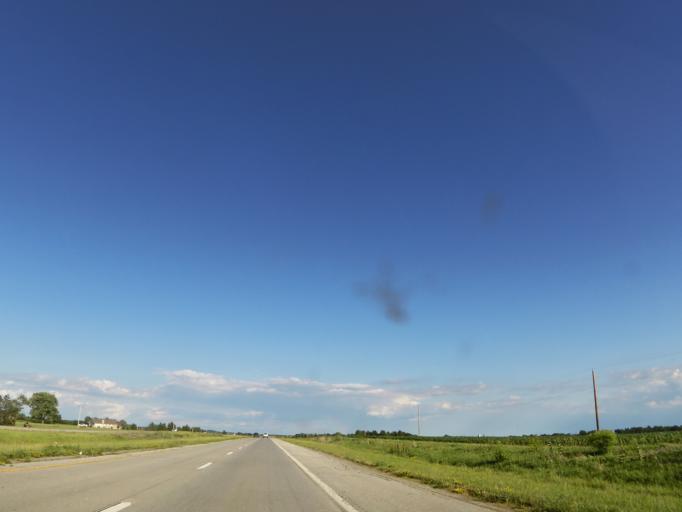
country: US
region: Missouri
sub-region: Pike County
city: Bowling Green
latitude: 39.3147
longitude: -91.1406
